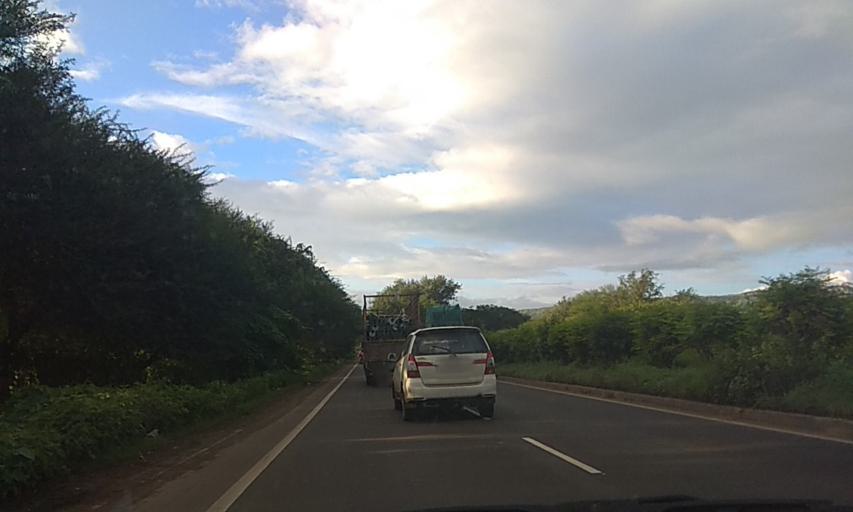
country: IN
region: Maharashtra
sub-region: Satara Division
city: Satara
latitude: 17.5729
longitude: 74.0505
